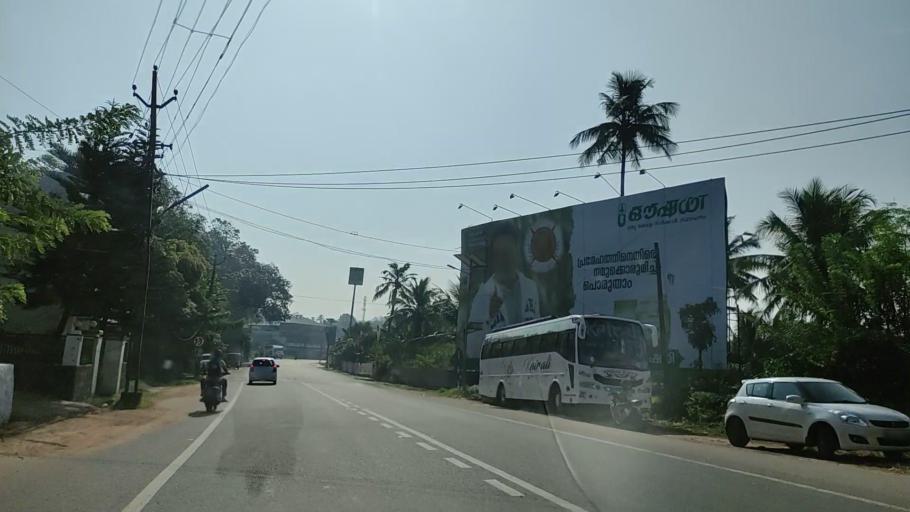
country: IN
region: Kerala
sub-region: Kollam
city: Punalur
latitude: 8.8767
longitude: 76.8677
